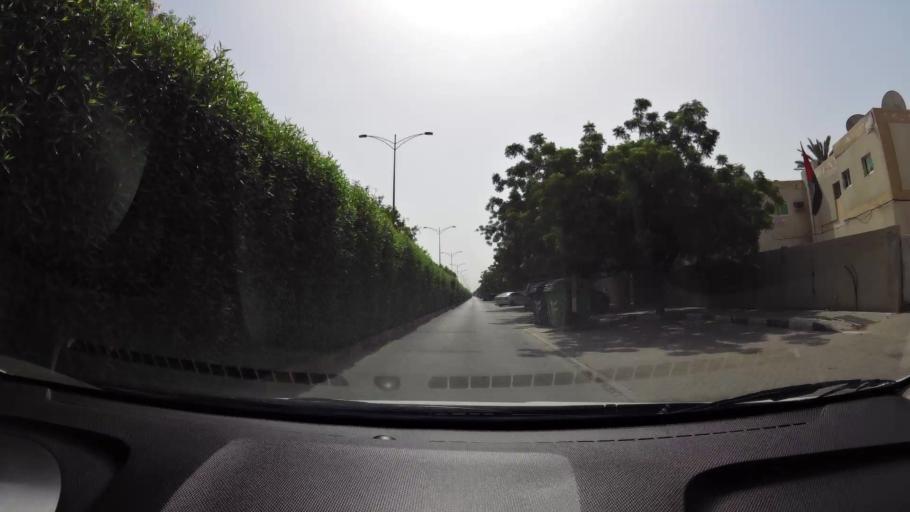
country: AE
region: Ash Shariqah
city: Sharjah
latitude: 25.3539
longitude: 55.4152
